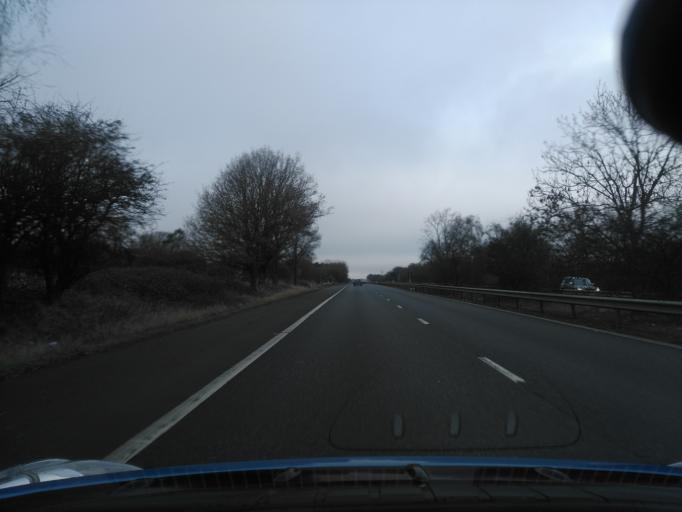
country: GB
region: England
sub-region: Hertfordshire
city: Stevenage
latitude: 51.8946
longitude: -0.2128
